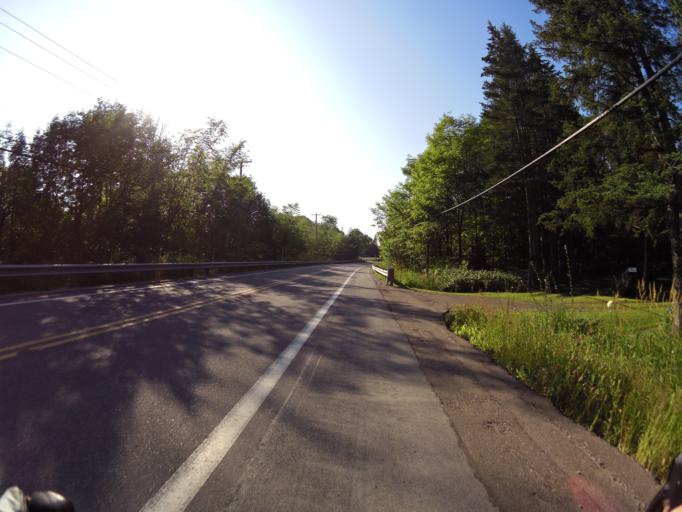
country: CA
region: Quebec
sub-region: Outaouais
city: Wakefield
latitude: 45.5551
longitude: -75.8304
